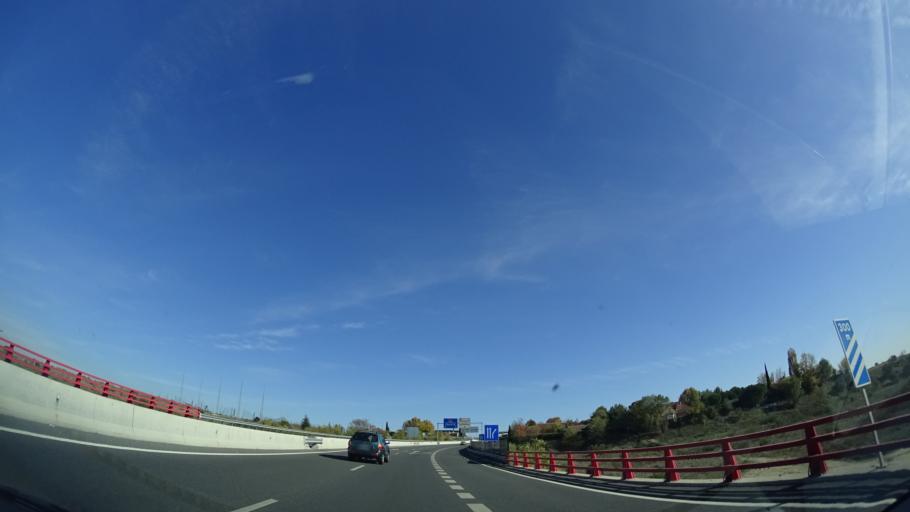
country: ES
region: Madrid
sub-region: Provincia de Madrid
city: Villanueva del Pardillo
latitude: 40.4849
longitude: -3.9366
